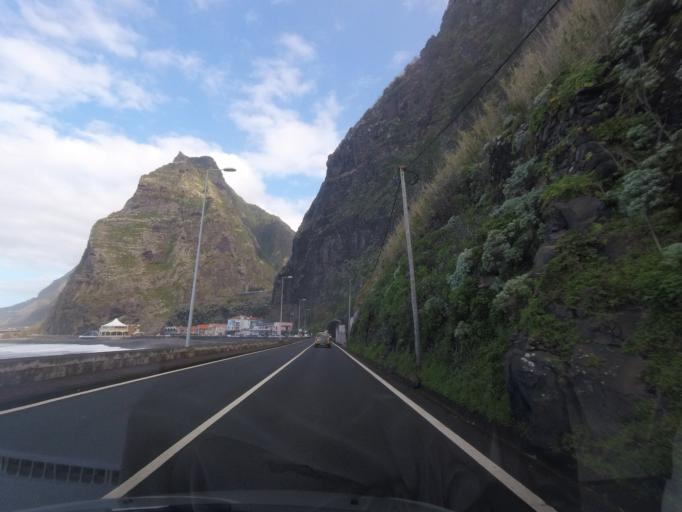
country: PT
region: Madeira
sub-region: Sao Vicente
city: Sao Vicente
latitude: 32.8087
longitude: -17.0523
